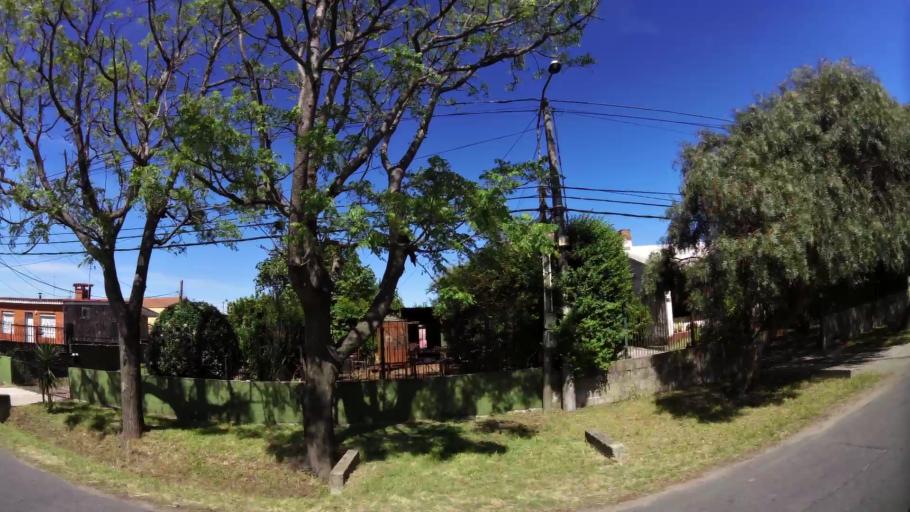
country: UY
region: Canelones
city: Paso de Carrasco
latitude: -34.8622
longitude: -56.1119
